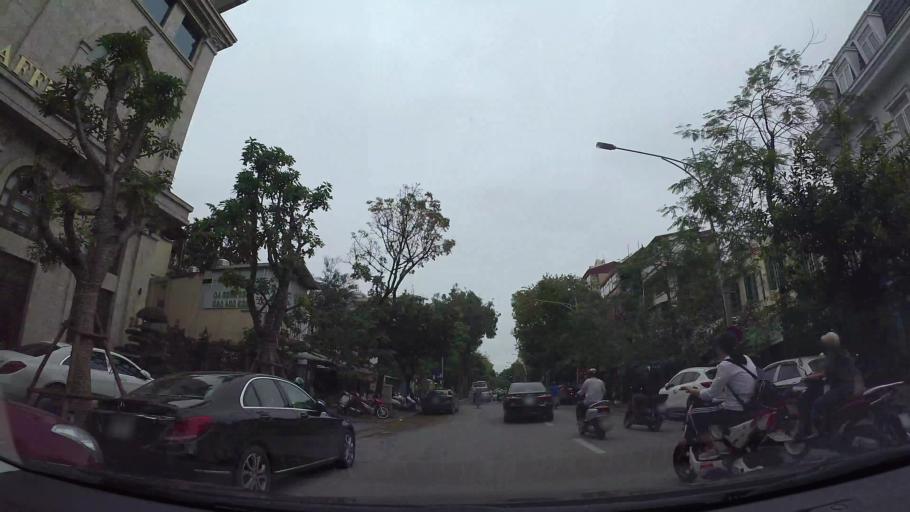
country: VN
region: Ha Noi
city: Hai BaTrung
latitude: 21.0211
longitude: 105.8483
